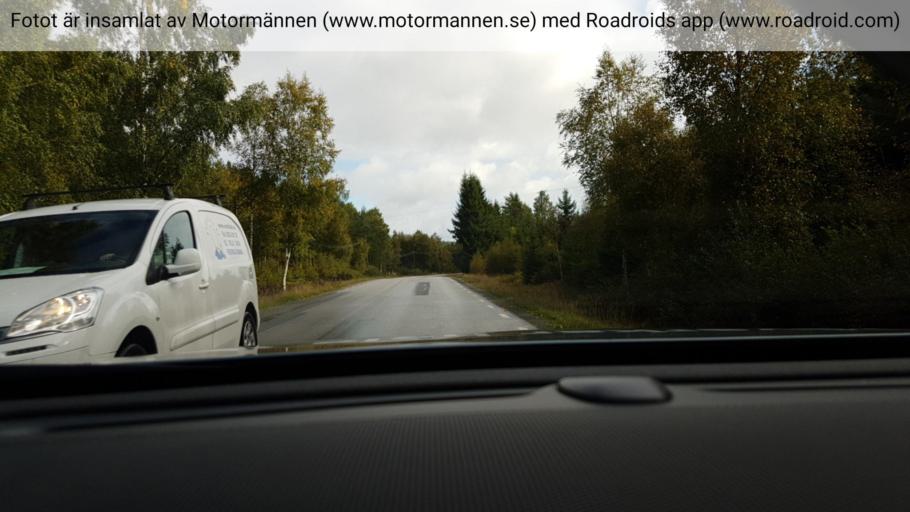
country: SE
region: Vaestra Goetaland
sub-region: Marks Kommun
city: Fritsla
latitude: 57.4014
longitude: 12.8386
